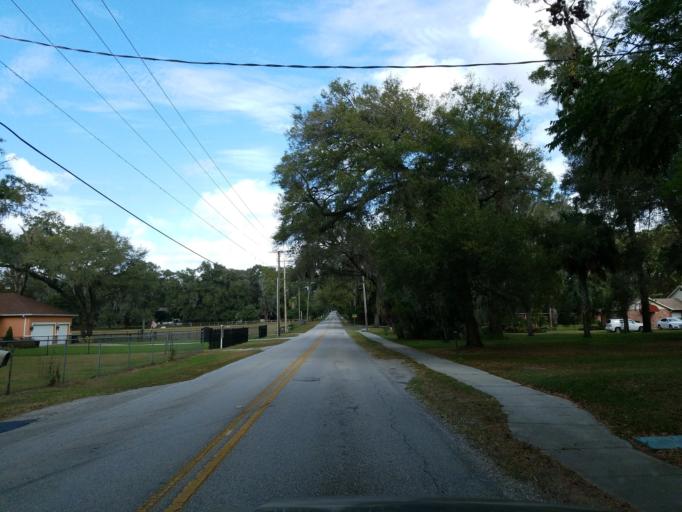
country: US
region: Florida
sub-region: Hillsborough County
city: Bloomingdale
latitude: 27.8992
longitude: -82.2198
